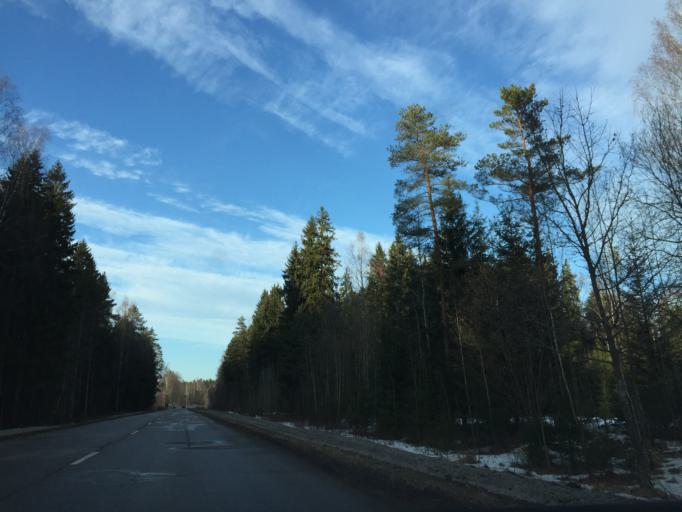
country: LV
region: Kekava
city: Balozi
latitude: 56.7464
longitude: 24.1077
